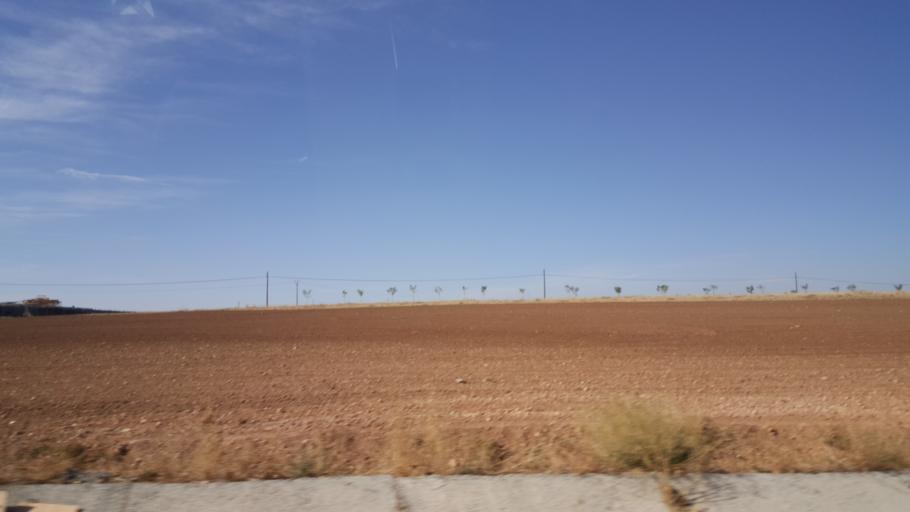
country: TR
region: Ankara
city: Ikizce
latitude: 39.5876
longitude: 32.6603
